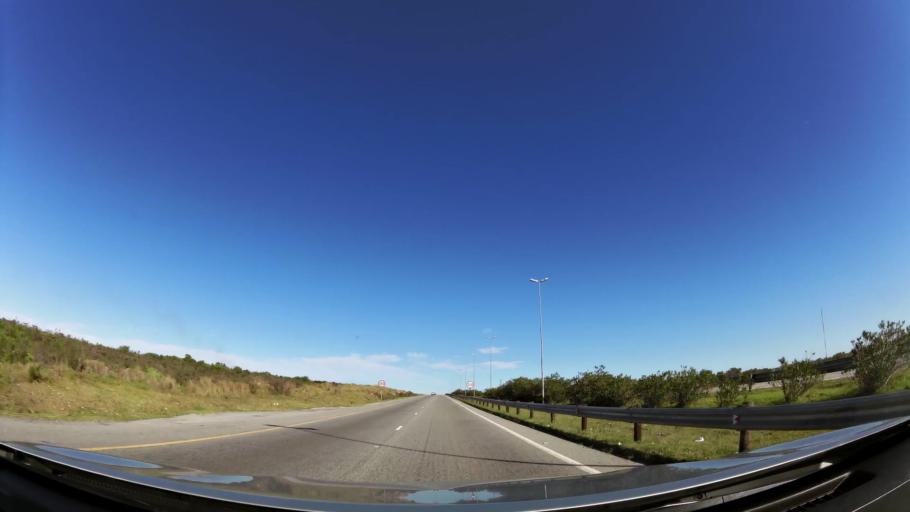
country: ZA
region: Eastern Cape
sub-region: Nelson Mandela Bay Metropolitan Municipality
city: Port Elizabeth
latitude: -33.9480
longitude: 25.4555
